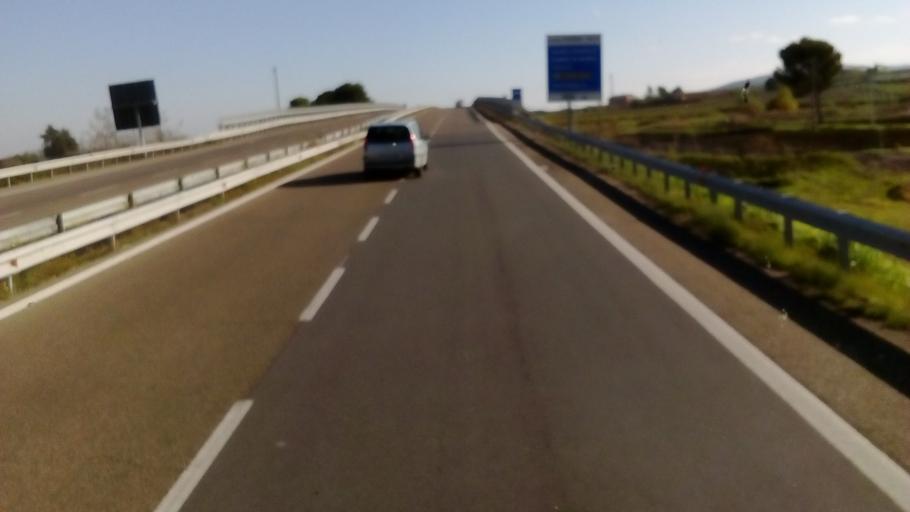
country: IT
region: Basilicate
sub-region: Provincia di Potenza
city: Zona 179
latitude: 41.0866
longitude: 15.5997
